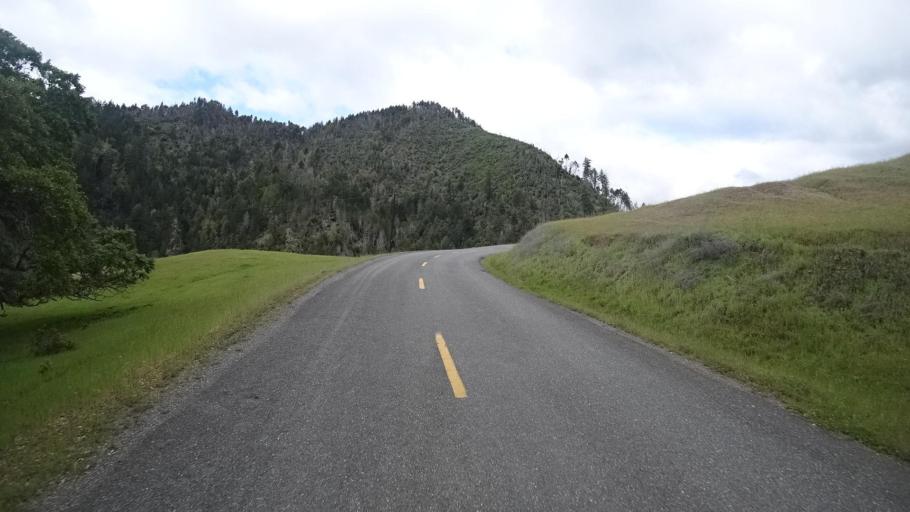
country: US
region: California
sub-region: Humboldt County
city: Redway
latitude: 40.2264
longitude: -123.6089
